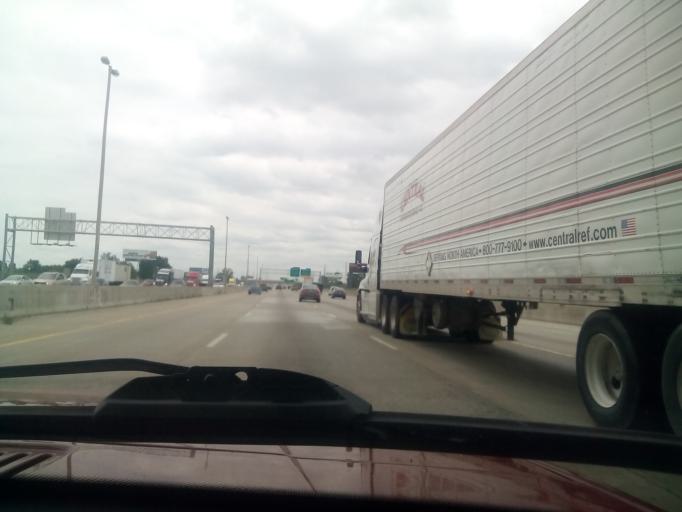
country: US
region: Indiana
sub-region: Lake County
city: Gary
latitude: 41.5673
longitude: -87.3269
